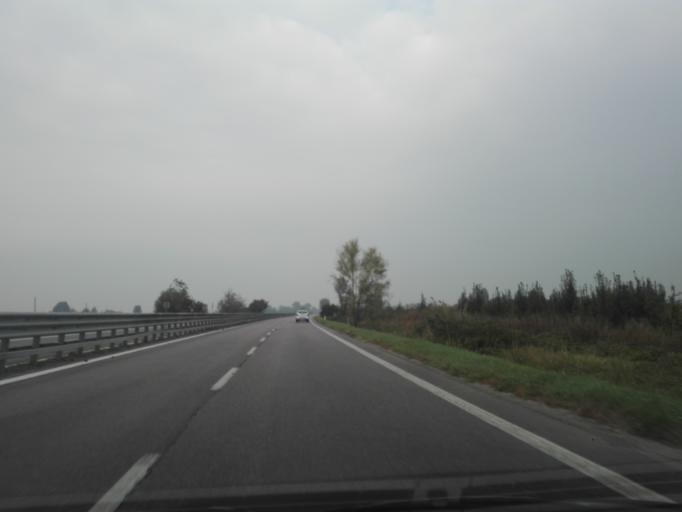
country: IT
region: Veneto
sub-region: Provincia di Verona
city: Villa Bartolomea
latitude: 45.1549
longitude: 11.3251
